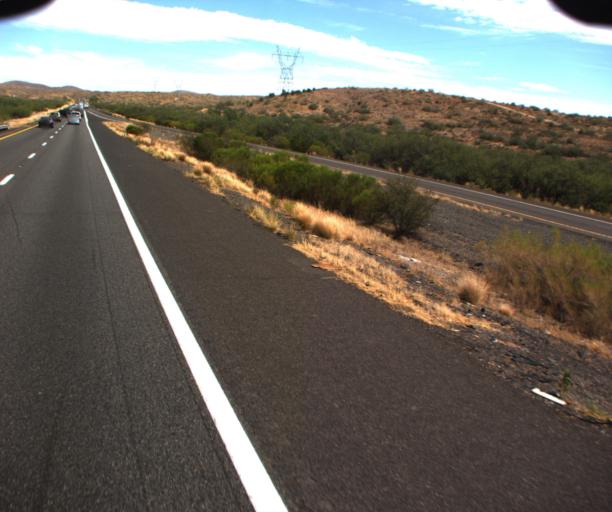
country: US
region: Arizona
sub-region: Yavapai County
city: Cordes Lakes
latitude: 34.2385
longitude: -112.1117
